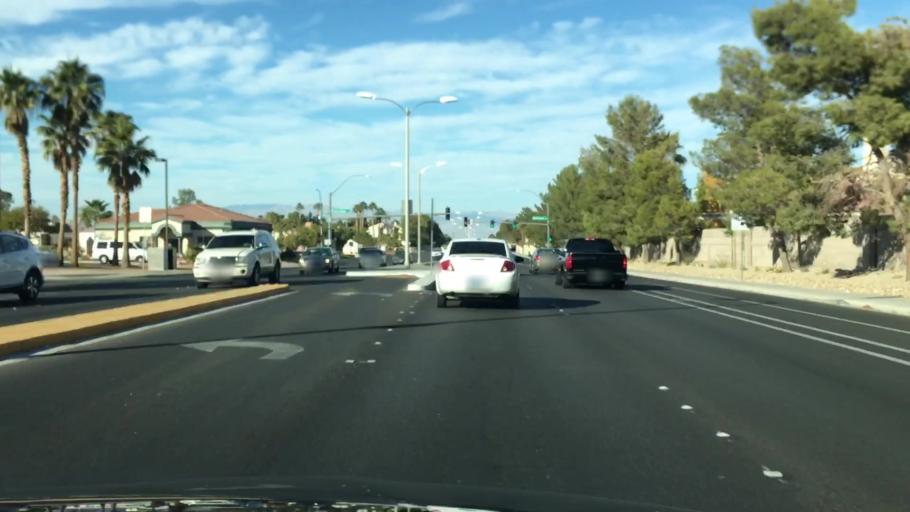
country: US
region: Nevada
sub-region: Clark County
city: Whitney
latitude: 36.0486
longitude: -115.1003
